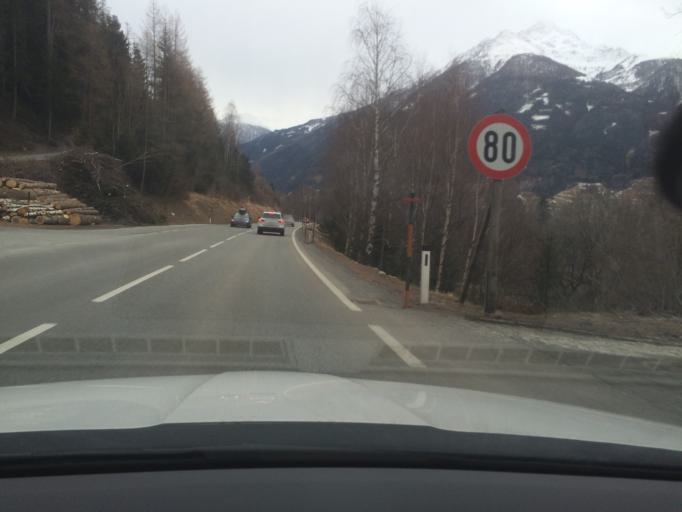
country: AT
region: Tyrol
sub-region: Politischer Bezirk Lienz
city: Matrei in Osttirol
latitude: 47.0108
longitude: 12.5396
